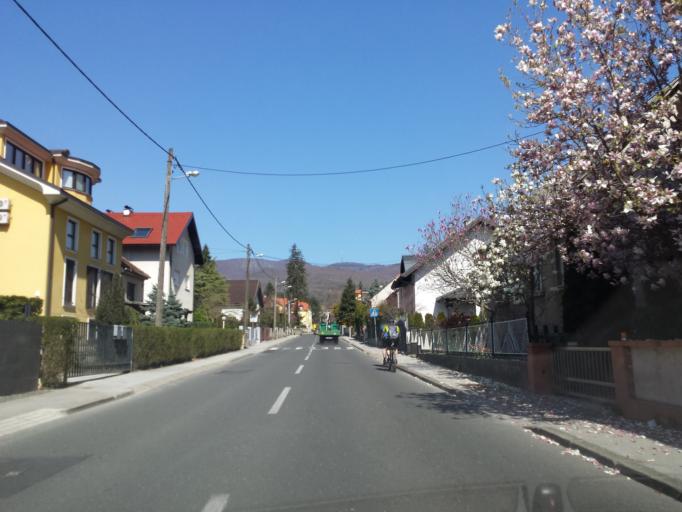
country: HR
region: Grad Zagreb
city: Zagreb
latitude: 45.8489
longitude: 15.9763
